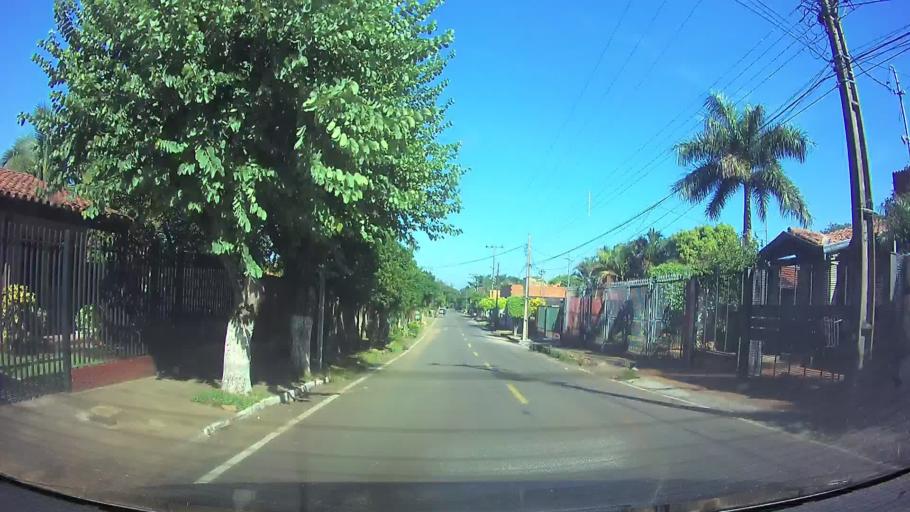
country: PY
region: Central
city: San Lorenzo
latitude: -25.2783
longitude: -57.5097
